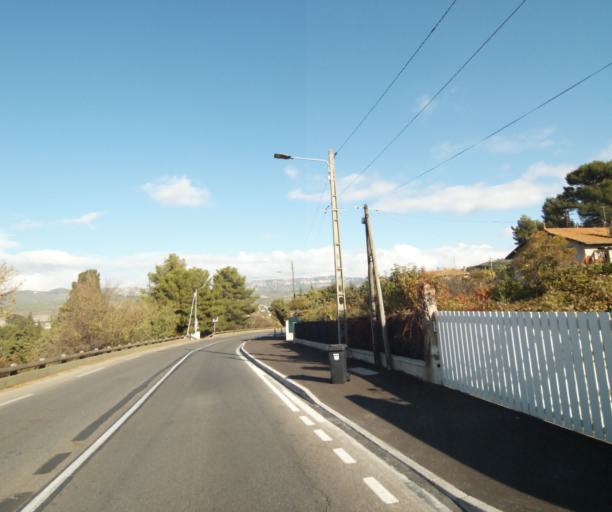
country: FR
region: Provence-Alpes-Cote d'Azur
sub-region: Departement des Bouches-du-Rhone
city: Allauch
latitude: 43.3435
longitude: 5.4862
